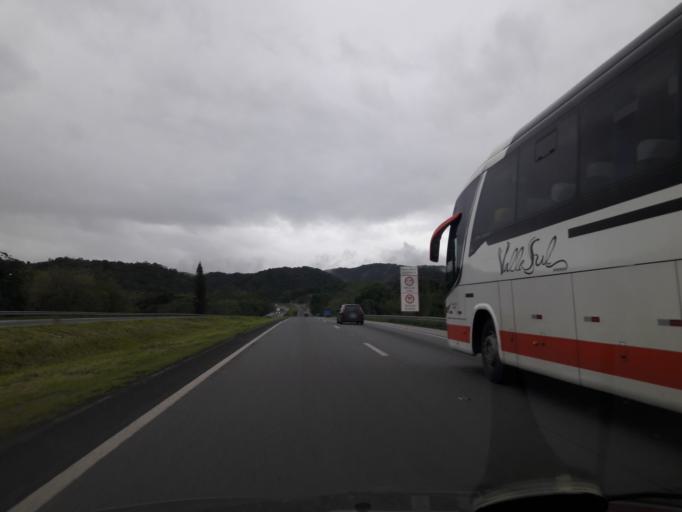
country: BR
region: Sao Paulo
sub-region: Miracatu
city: Miracatu
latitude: -24.2467
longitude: -47.3689
